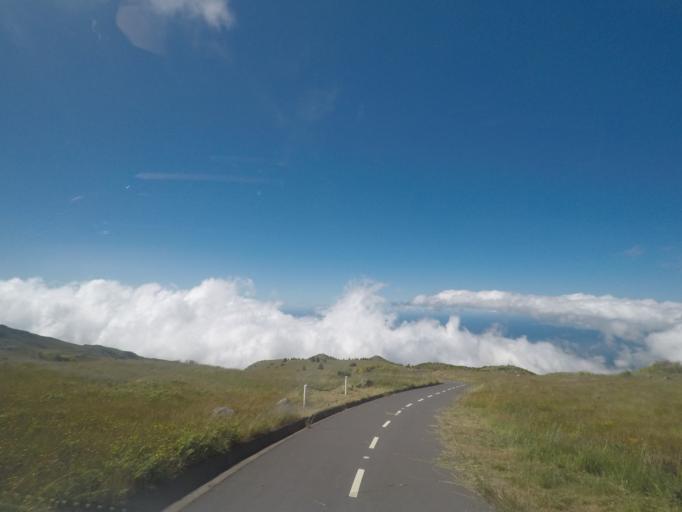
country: PT
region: Madeira
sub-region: Camara de Lobos
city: Curral das Freiras
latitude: 32.7124
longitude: -16.9384
